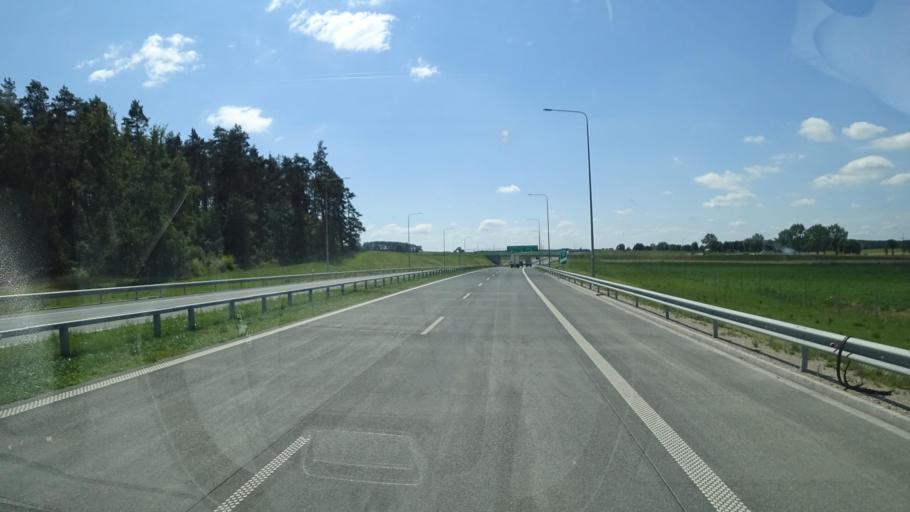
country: PL
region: Podlasie
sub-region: Powiat kolnenski
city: Stawiski
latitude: 53.4612
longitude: 22.2009
